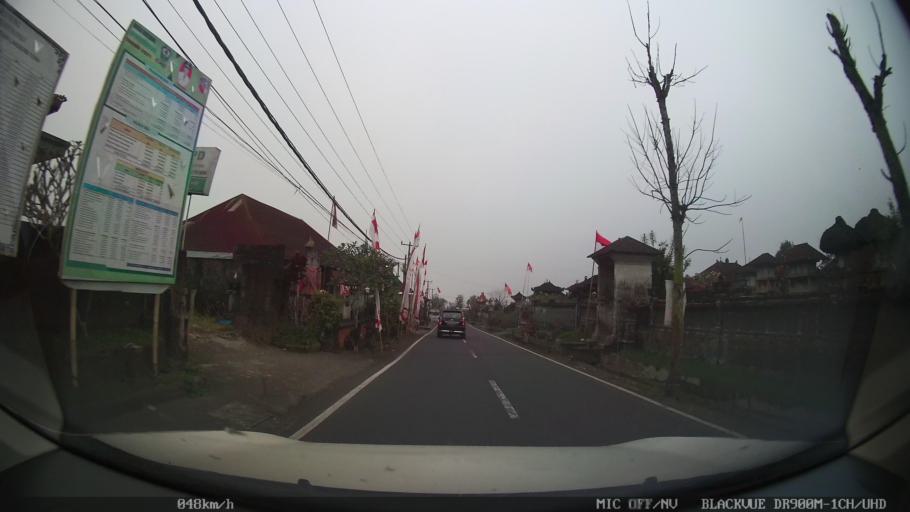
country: ID
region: Bali
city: Banjar Taro Kelod
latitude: -8.3094
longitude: 115.3048
